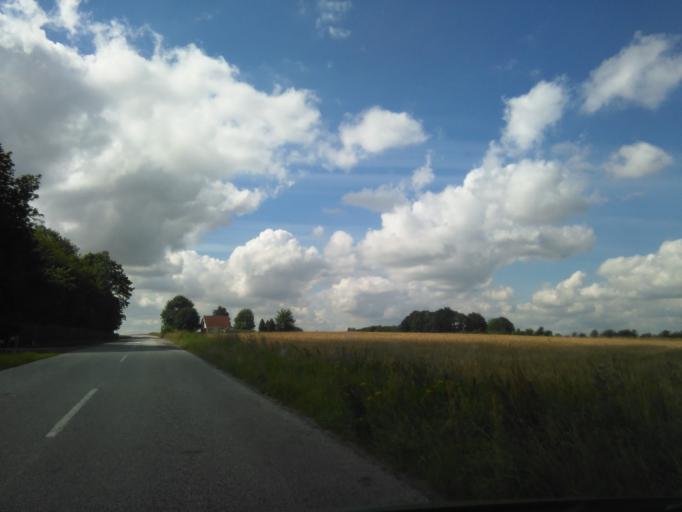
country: DK
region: Central Jutland
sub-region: Arhus Kommune
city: Solbjerg
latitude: 56.0582
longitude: 10.0890
